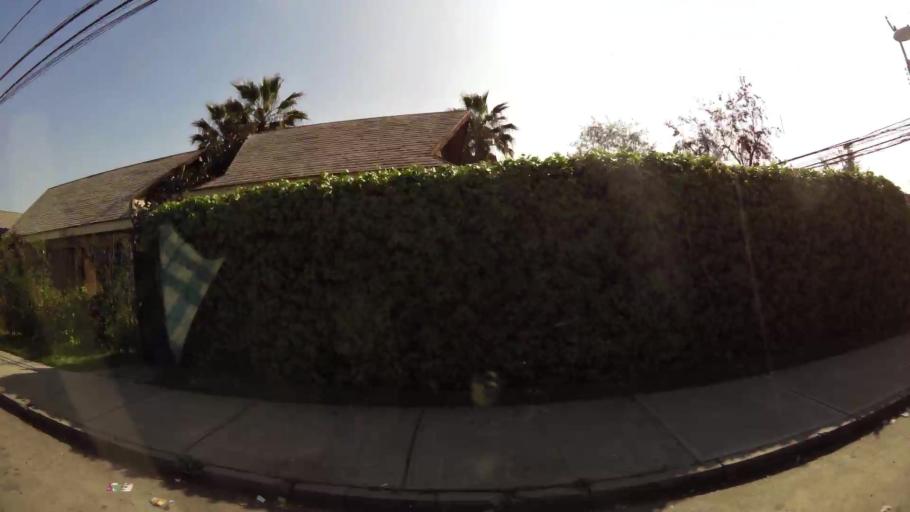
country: CL
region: Santiago Metropolitan
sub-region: Provincia de Santiago
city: Villa Presidente Frei, Nunoa, Santiago, Chile
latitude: -33.3940
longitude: -70.5701
